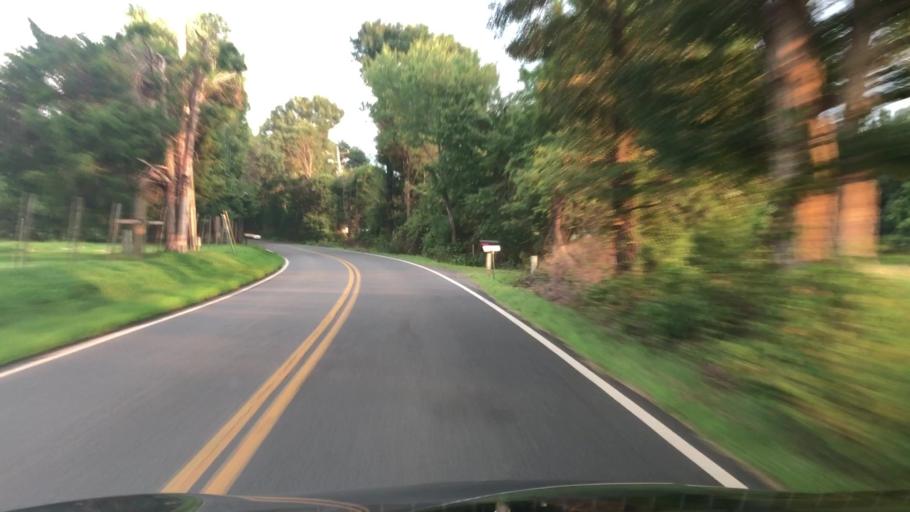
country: US
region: Virginia
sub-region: Fauquier County
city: Bealeton
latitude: 38.5408
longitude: -77.6758
